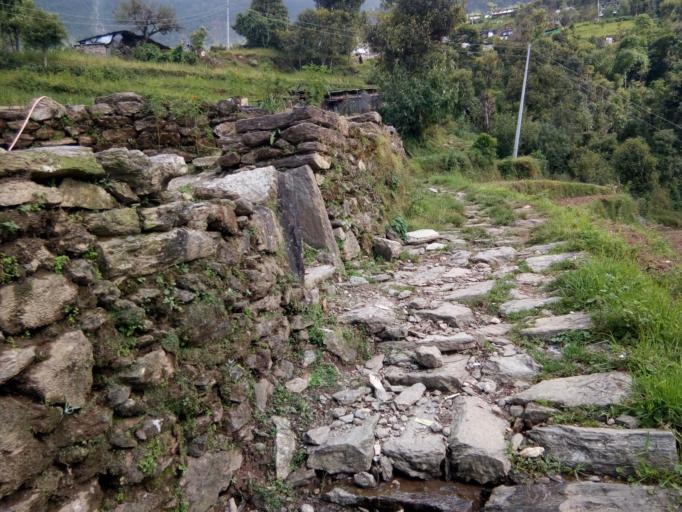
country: NP
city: Kodari
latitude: 27.7039
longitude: 85.9200
